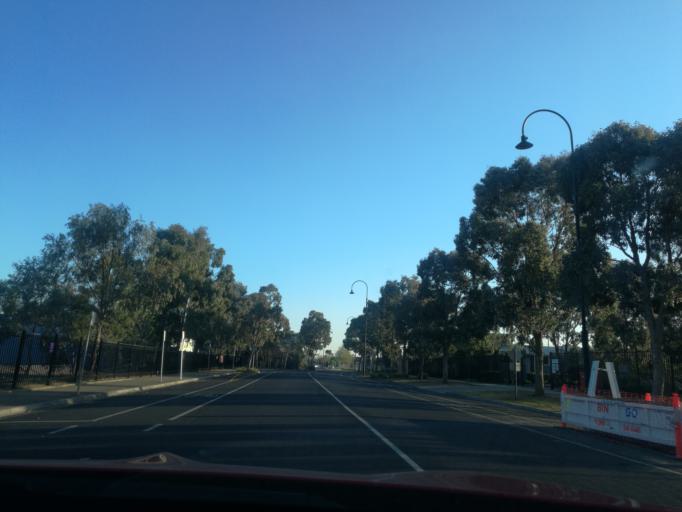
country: AU
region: Victoria
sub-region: Wyndham
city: Williams Landing
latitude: -37.8848
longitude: 144.7433
